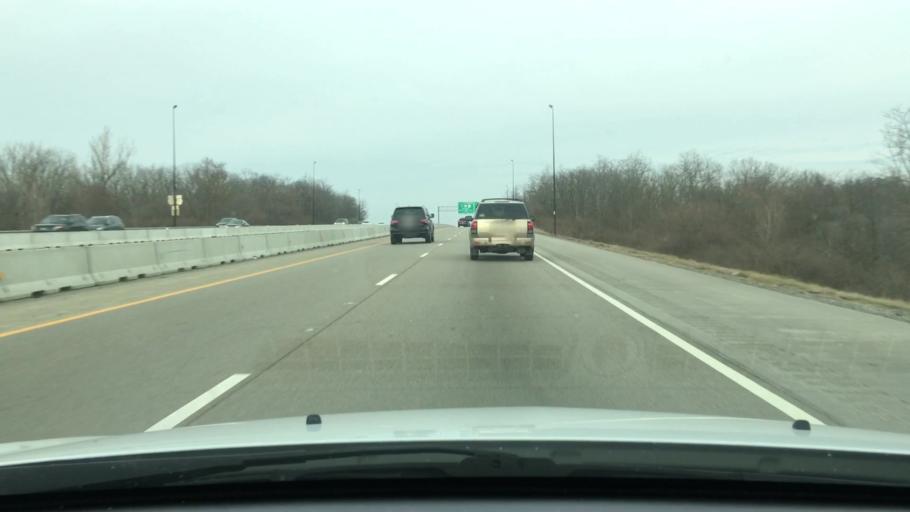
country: US
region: Illinois
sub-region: Sangamon County
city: Grandview
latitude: 39.7801
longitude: -89.6009
